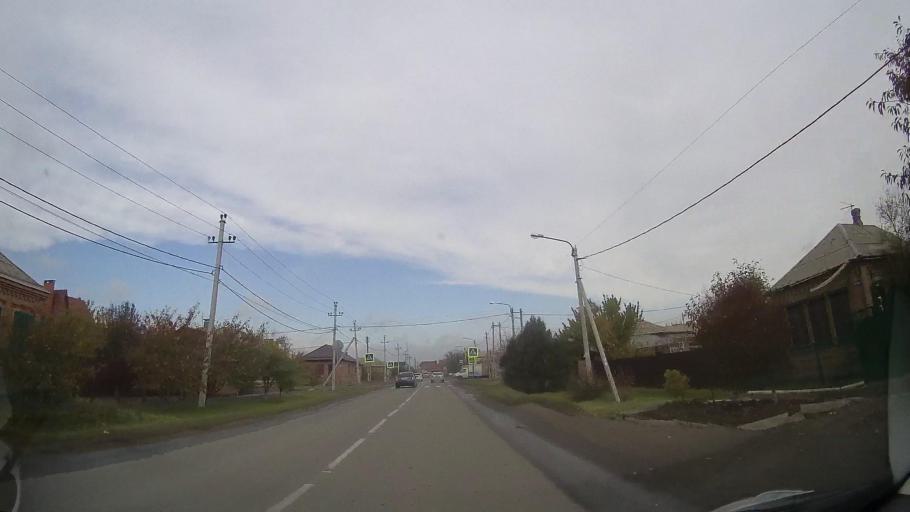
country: RU
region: Rostov
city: Bataysk
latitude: 47.1479
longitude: 39.7669
